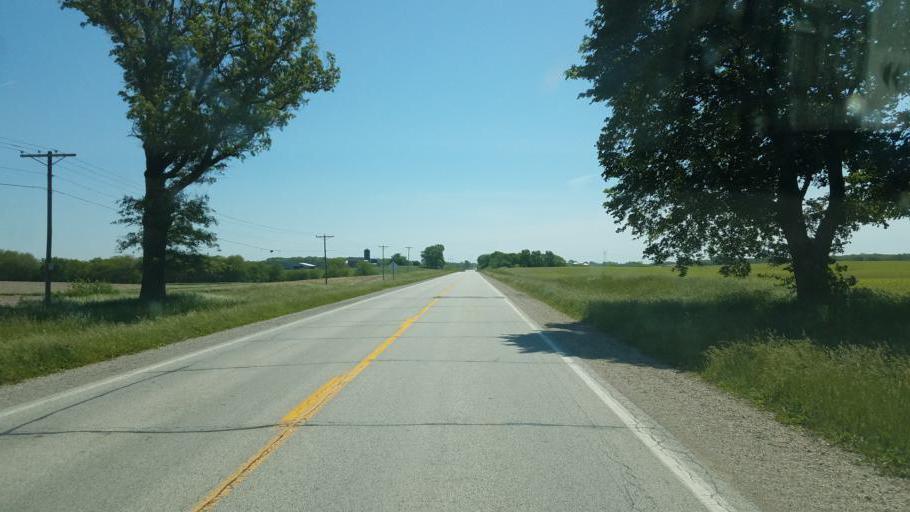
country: US
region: Illinois
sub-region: McLean County
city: Heyworth
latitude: 40.3121
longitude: -89.0347
